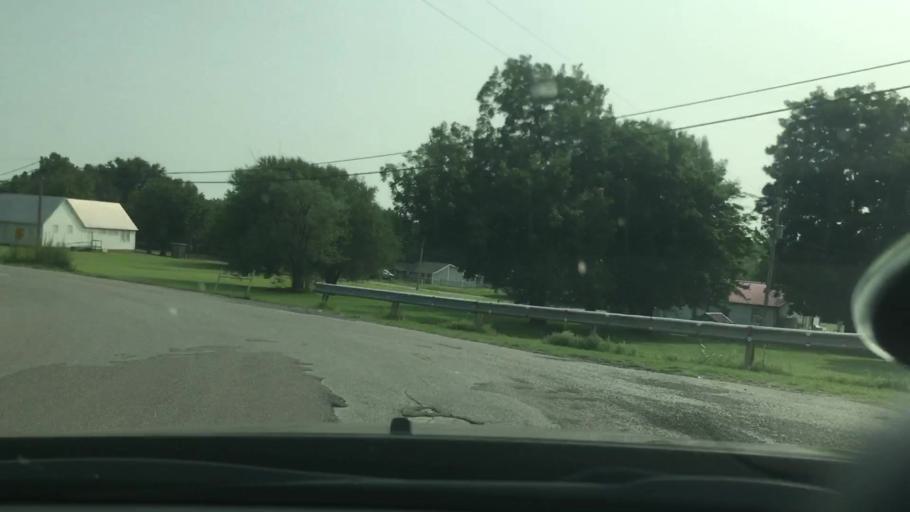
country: US
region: Oklahoma
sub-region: Garvin County
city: Lindsay
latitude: 34.8101
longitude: -97.6082
